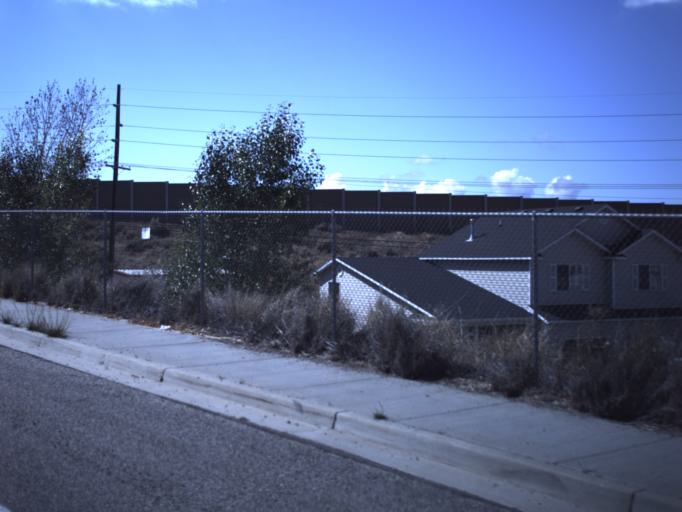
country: US
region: Utah
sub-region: Utah County
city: Spanish Fork
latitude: 40.1165
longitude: -111.6349
